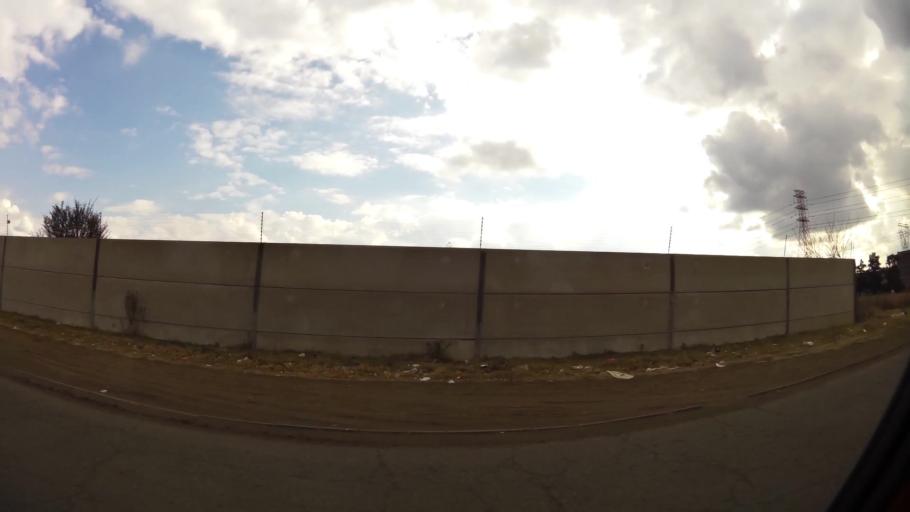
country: ZA
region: Gauteng
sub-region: Sedibeng District Municipality
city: Vanderbijlpark
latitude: -26.6746
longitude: 27.8181
